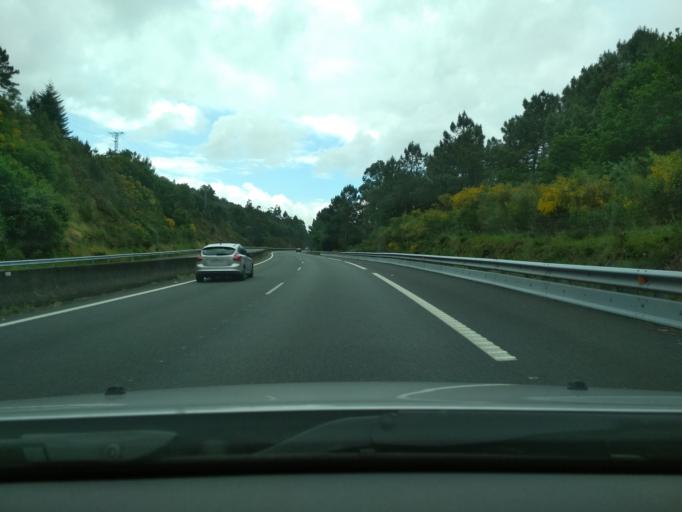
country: ES
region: Galicia
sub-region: Provincia da Coruna
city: Padron
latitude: 42.7885
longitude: -8.6428
